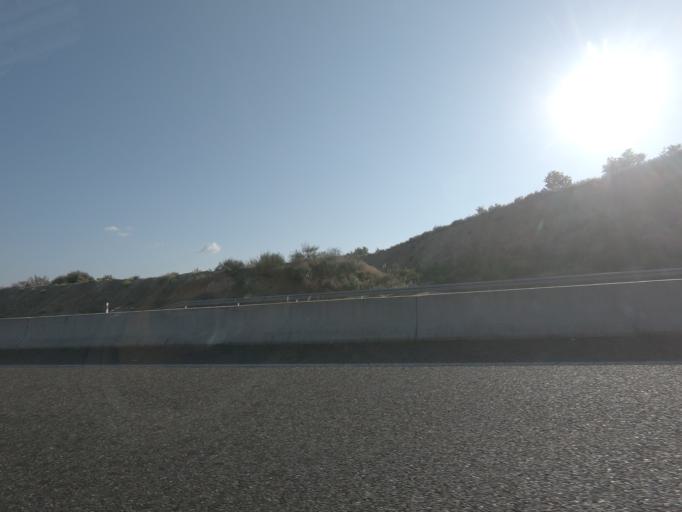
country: ES
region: Galicia
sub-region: Provincia de Ourense
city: Oimbra
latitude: 41.8256
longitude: -7.4202
